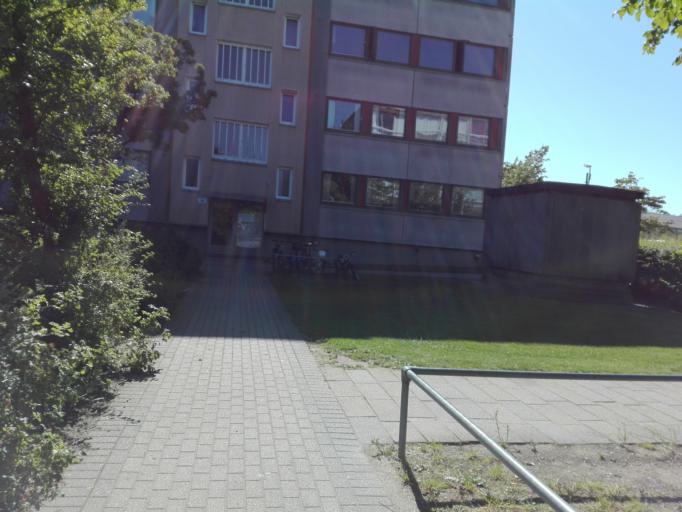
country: DK
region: Central Jutland
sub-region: Arhus Kommune
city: Stavtrup
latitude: 56.1129
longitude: 10.1494
